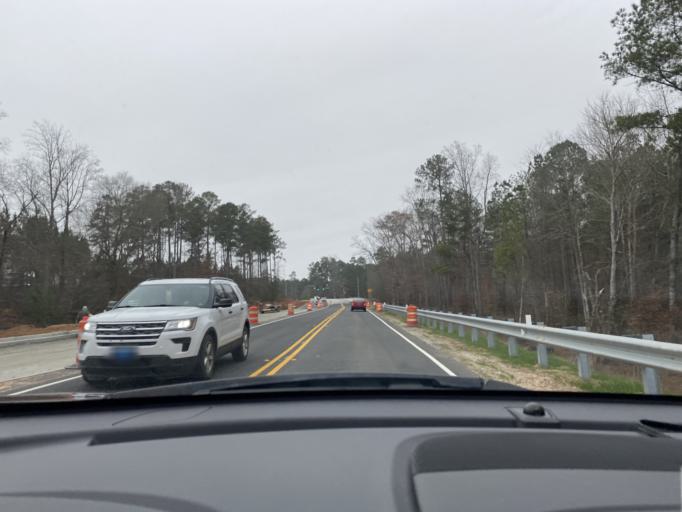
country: US
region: Georgia
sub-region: Gwinnett County
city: Grayson
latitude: 33.9177
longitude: -83.8914
